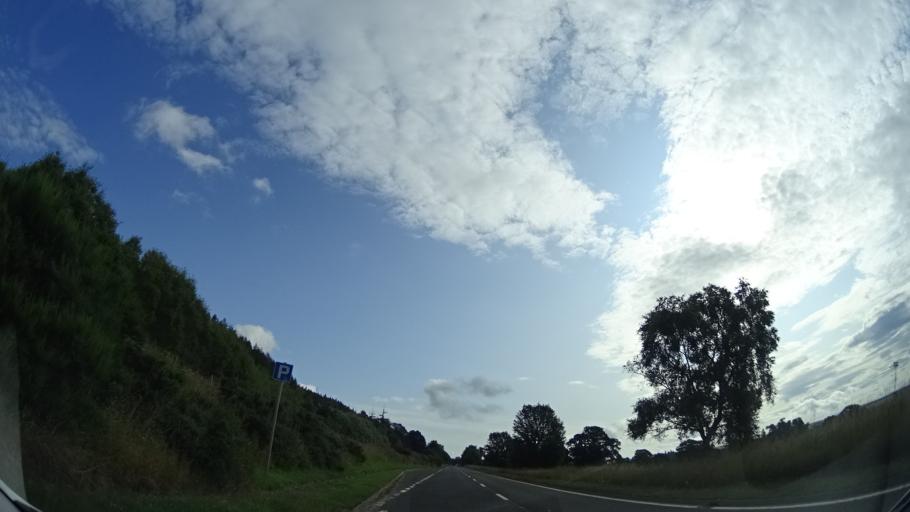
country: GB
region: Scotland
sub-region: Highland
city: Muir of Ord
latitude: 57.5601
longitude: -4.4967
